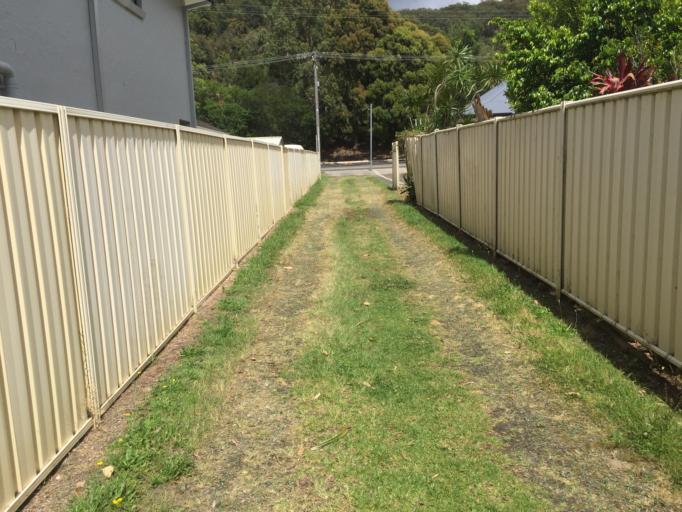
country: AU
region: New South Wales
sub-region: Gosford Shire
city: Point Clare
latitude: -33.4667
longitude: 151.3195
